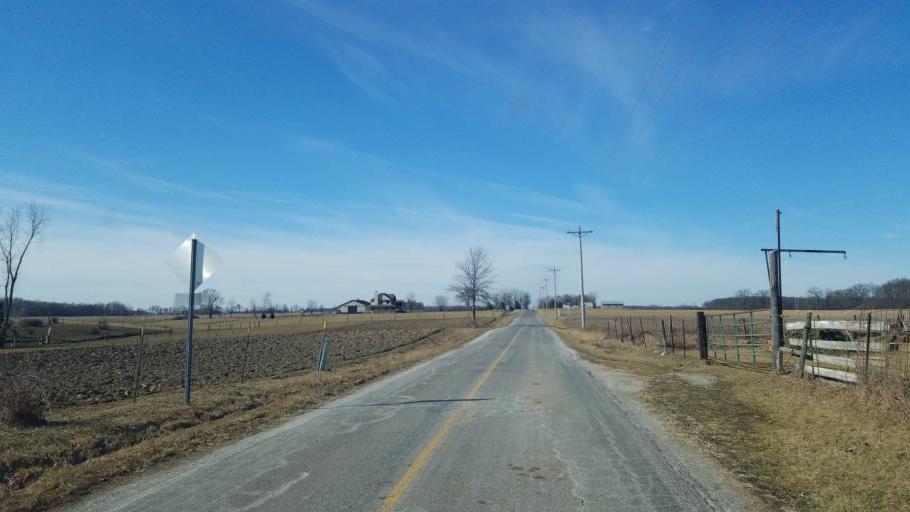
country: US
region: Ohio
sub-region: Union County
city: Richwood
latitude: 40.5450
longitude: -83.4153
